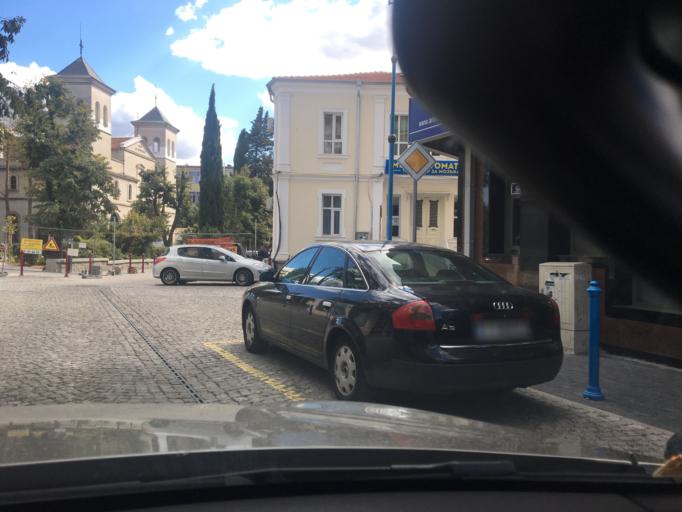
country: BG
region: Burgas
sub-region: Obshtina Burgas
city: Burgas
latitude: 42.4930
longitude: 27.4745
